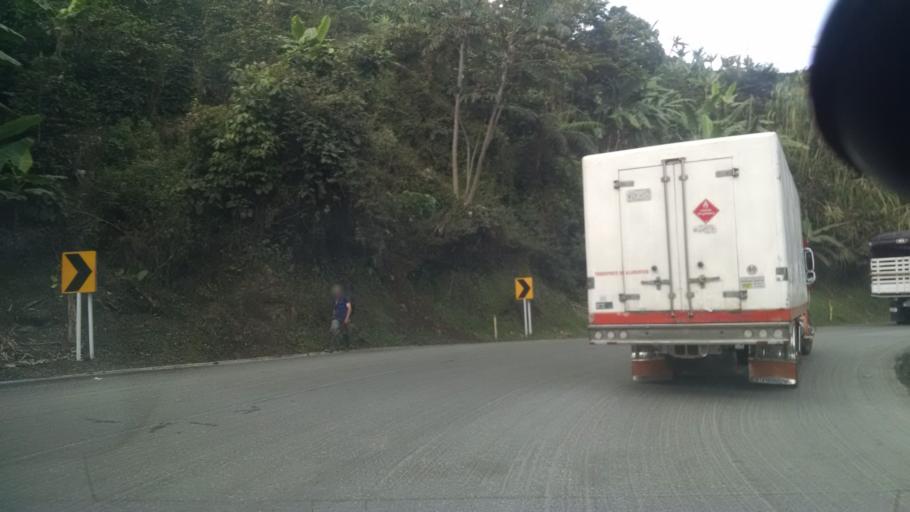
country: CO
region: Antioquia
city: Santa Barbara
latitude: 5.9003
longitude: -75.5729
